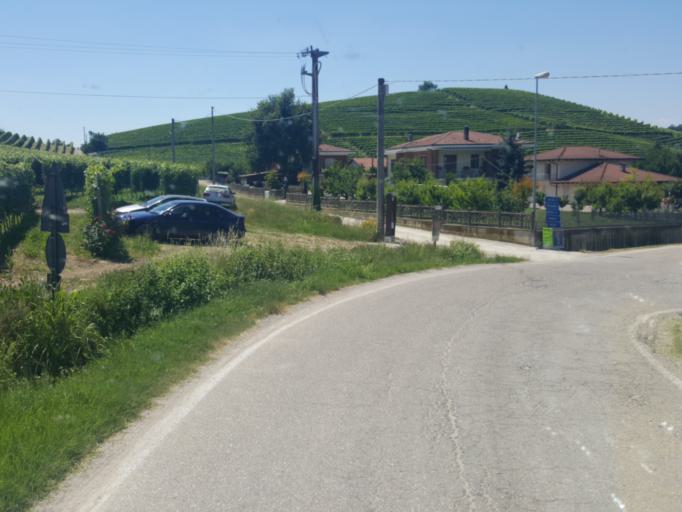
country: IT
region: Piedmont
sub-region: Provincia di Cuneo
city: Castagnito
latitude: 44.7633
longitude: 8.0302
